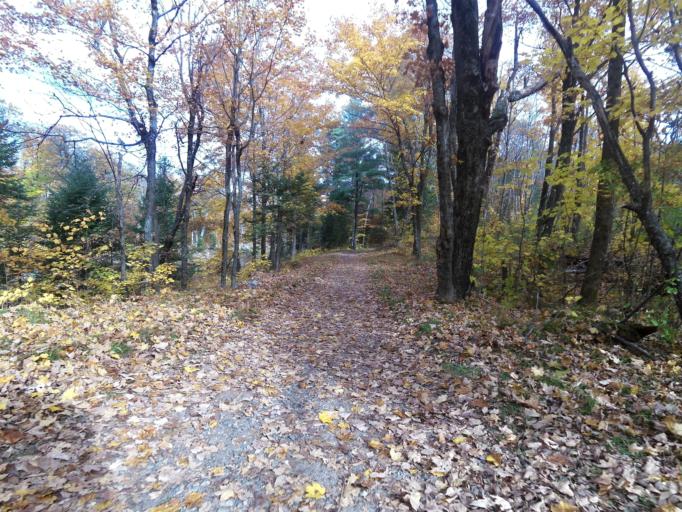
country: CA
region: Quebec
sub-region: Outaouais
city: Wakefield
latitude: 45.5058
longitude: -75.8996
